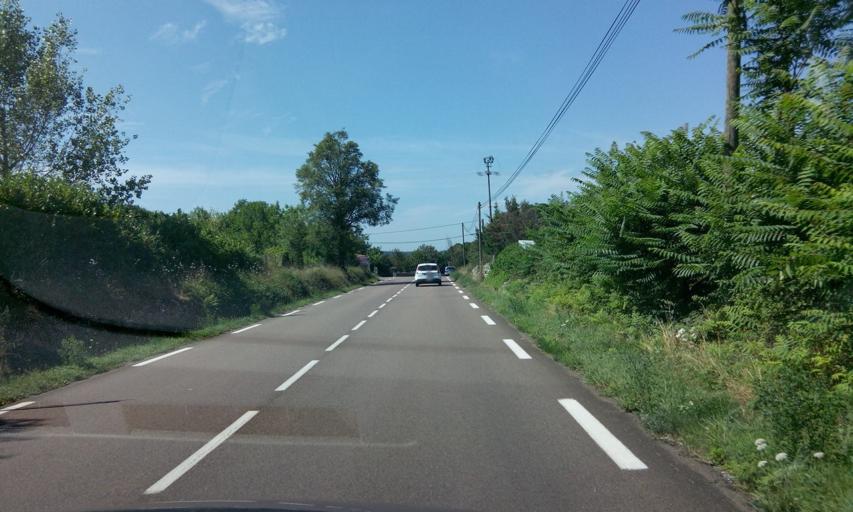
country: FR
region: Midi-Pyrenees
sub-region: Departement du Lot
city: Vayrac
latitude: 44.8728
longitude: 1.6246
